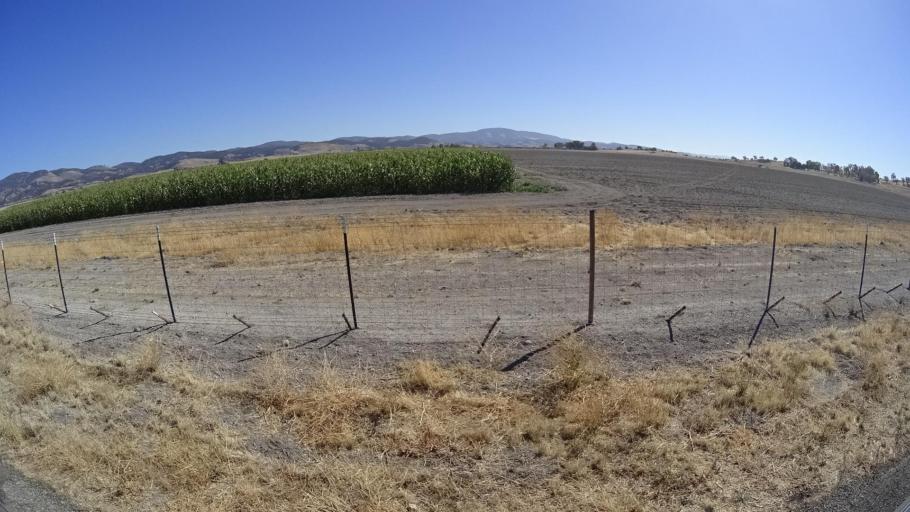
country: US
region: California
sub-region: Monterey County
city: King City
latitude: 35.9627
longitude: -121.1186
